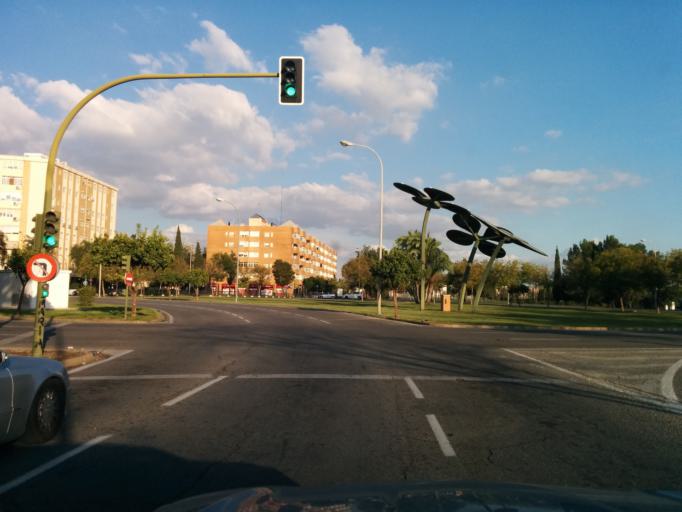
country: ES
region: Andalusia
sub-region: Provincia de Sevilla
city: Sevilla
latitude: 37.3871
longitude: -5.9208
